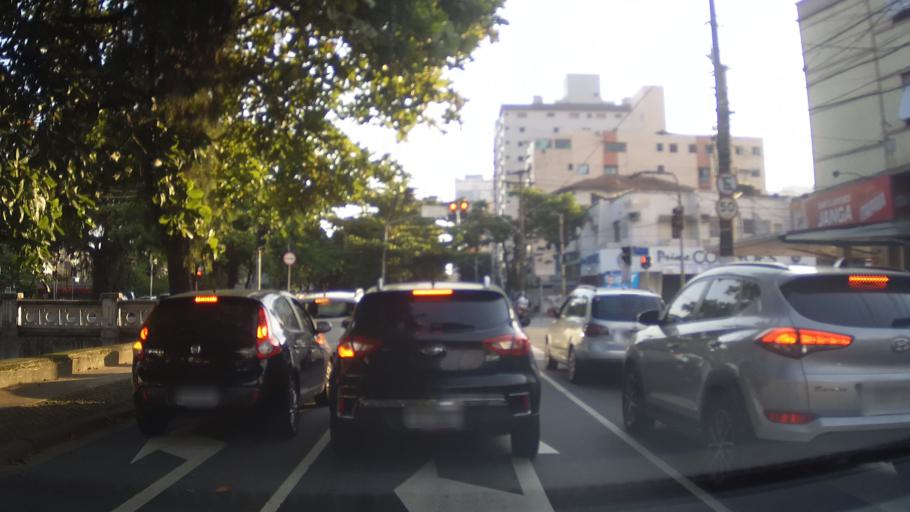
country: BR
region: Sao Paulo
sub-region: Santos
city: Santos
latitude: -23.9768
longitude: -46.3001
